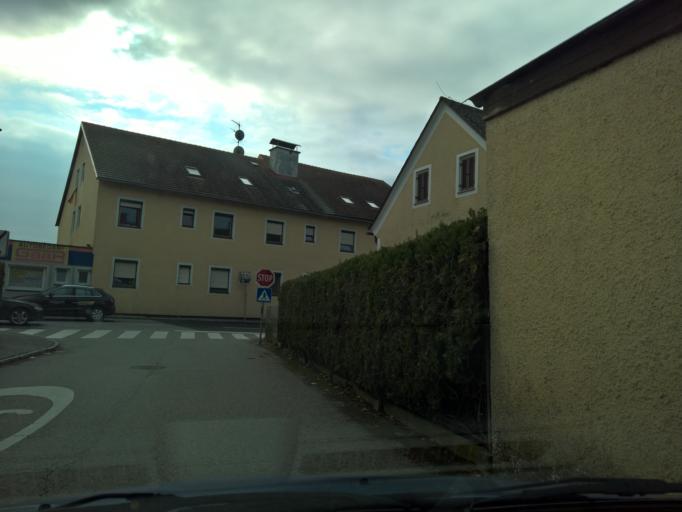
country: AT
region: Styria
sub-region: Politischer Bezirk Leibnitz
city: Kaindorf an der Sulm
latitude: 46.7872
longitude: 15.5468
